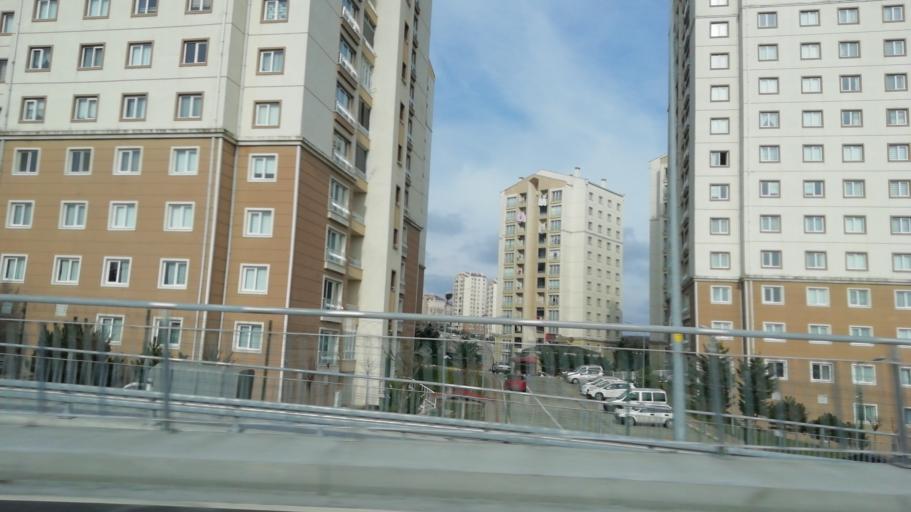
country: TR
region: Istanbul
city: Basaksehir
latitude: 41.1297
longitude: 28.7888
